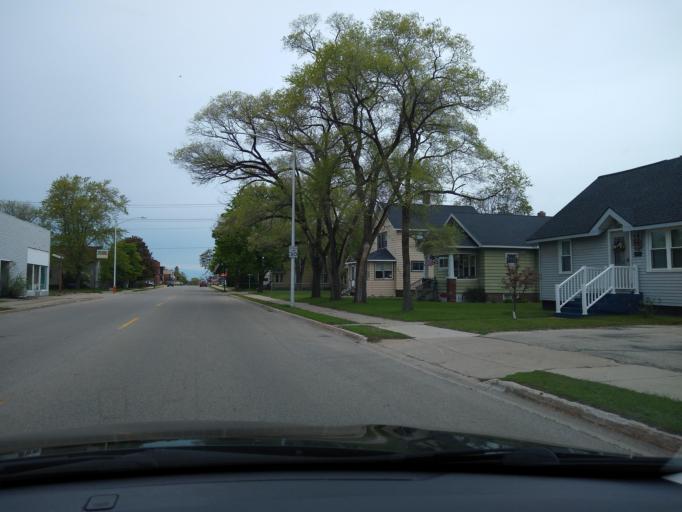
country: US
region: Michigan
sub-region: Delta County
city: Escanaba
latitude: 45.7627
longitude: -87.0691
